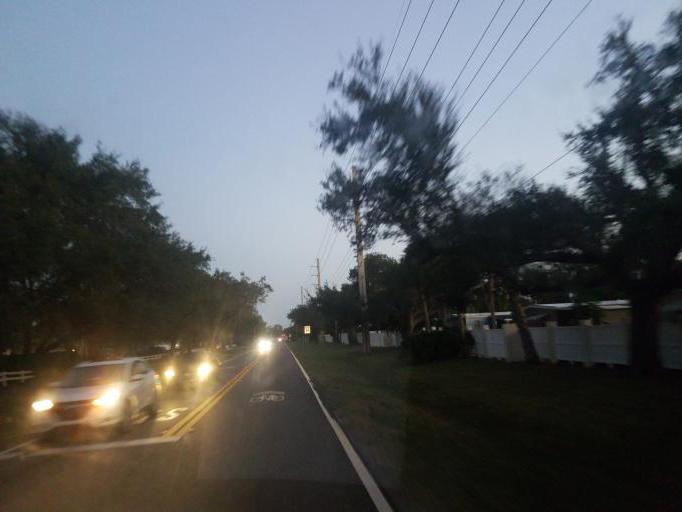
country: US
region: Florida
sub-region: Sarasota County
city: Lake Sarasota
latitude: 27.2765
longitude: -82.4563
